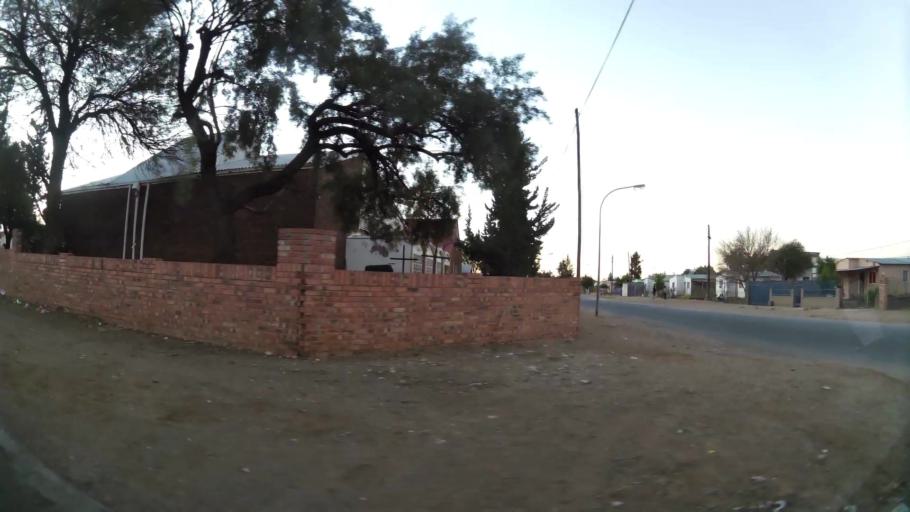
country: ZA
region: Northern Cape
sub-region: Frances Baard District Municipality
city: Kimberley
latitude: -28.7195
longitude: 24.7674
